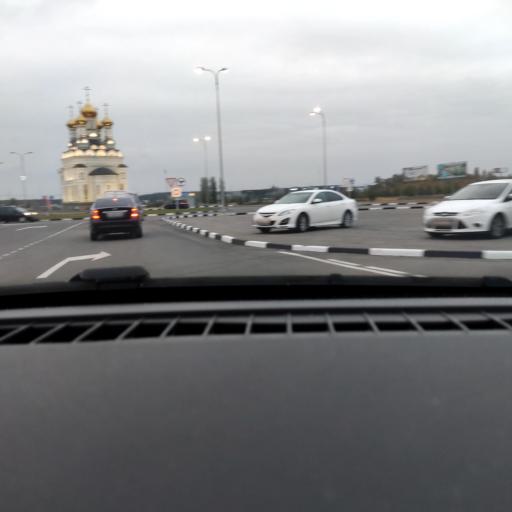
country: RU
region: Voronezj
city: Podgornoye
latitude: 51.7911
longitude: 39.2040
